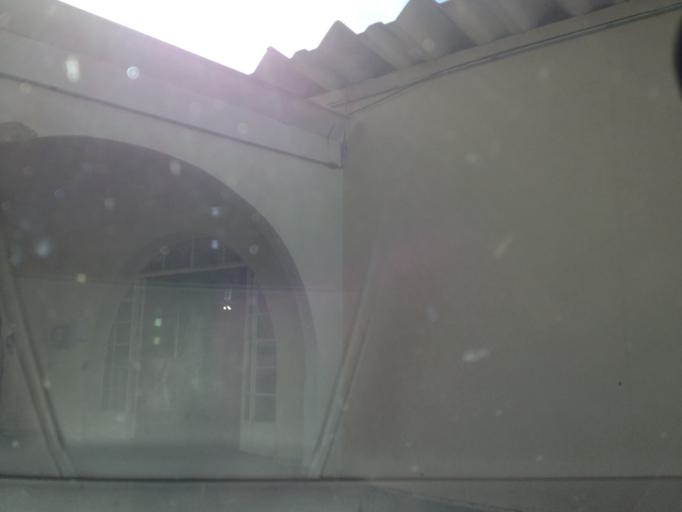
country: BR
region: Sao Paulo
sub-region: Marilia
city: Marilia
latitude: -22.1971
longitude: -49.9300
